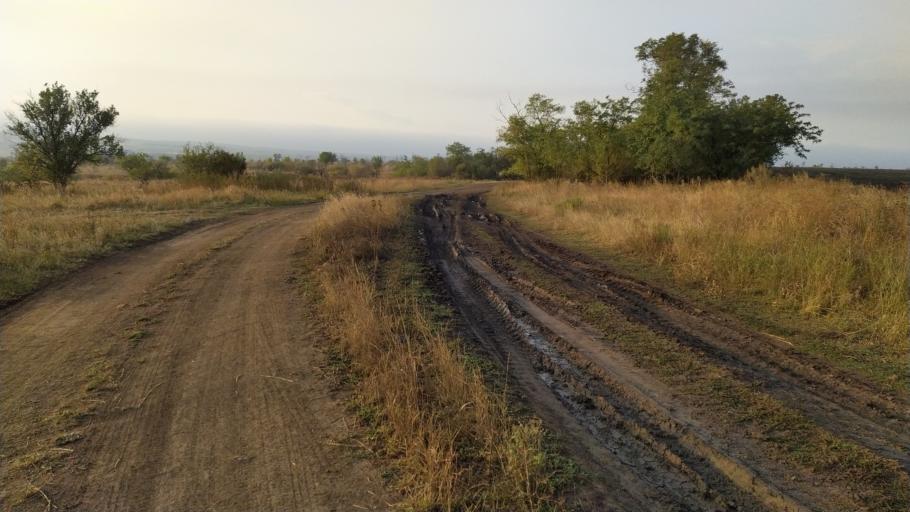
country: RU
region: Rostov
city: Gornyy
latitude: 47.8904
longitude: 40.2411
